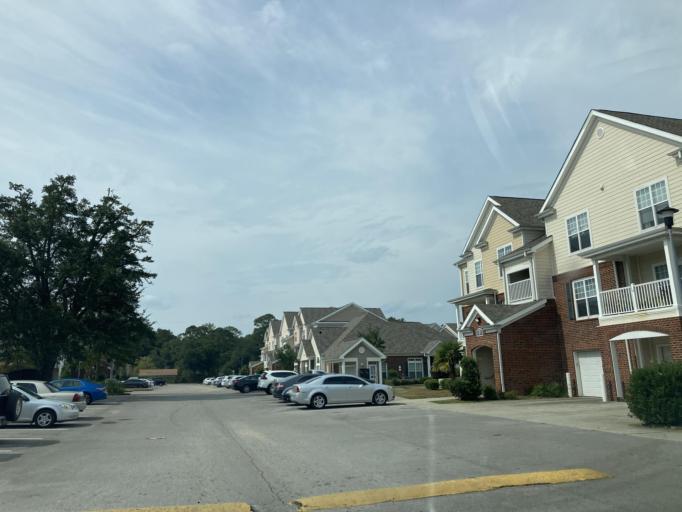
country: US
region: Mississippi
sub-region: Jackson County
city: Gulf Hills
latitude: 30.4510
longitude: -88.8440
